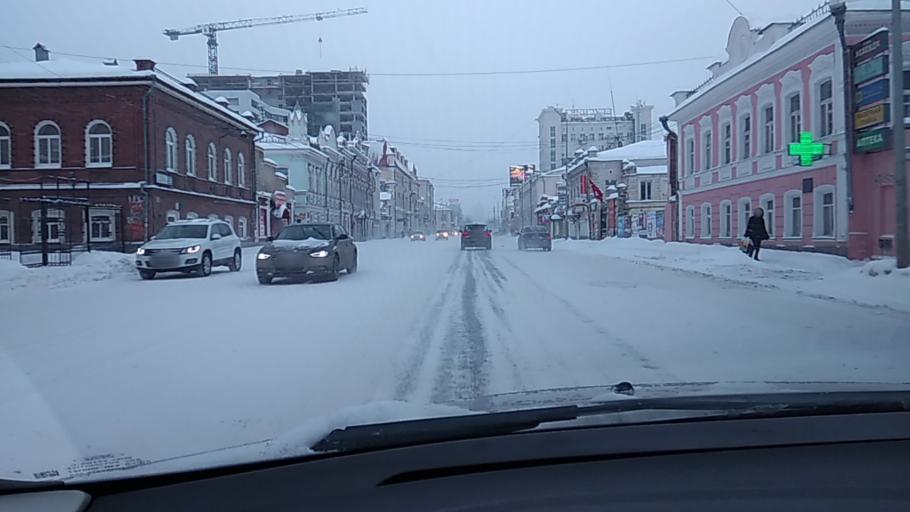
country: RU
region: Sverdlovsk
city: Yekaterinburg
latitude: 56.8315
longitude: 60.6008
